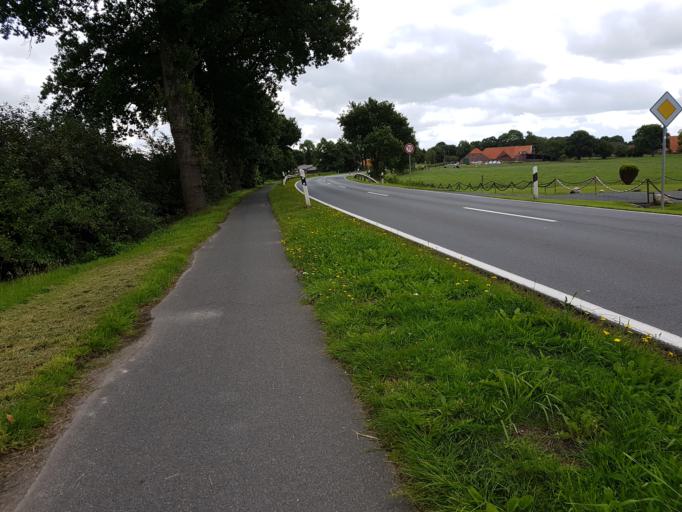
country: DE
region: Lower Saxony
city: Wittmund
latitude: 53.5213
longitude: 7.7890
